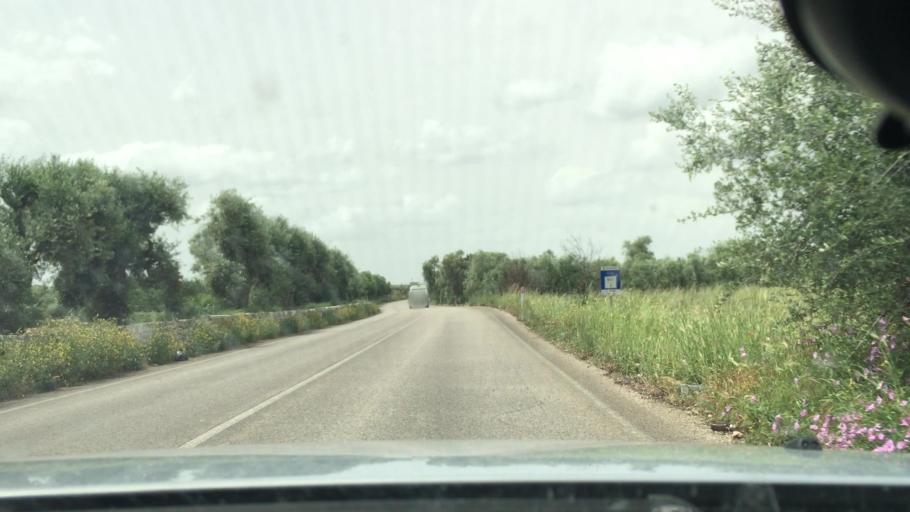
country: IT
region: Apulia
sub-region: Provincia di Bari
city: Capurso
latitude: 41.0423
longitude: 16.9422
